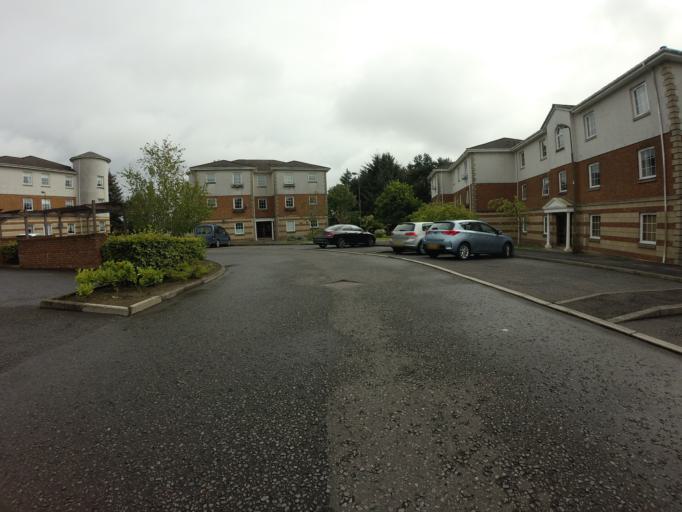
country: GB
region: Scotland
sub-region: West Lothian
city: Livingston
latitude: 55.9105
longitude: -3.5358
